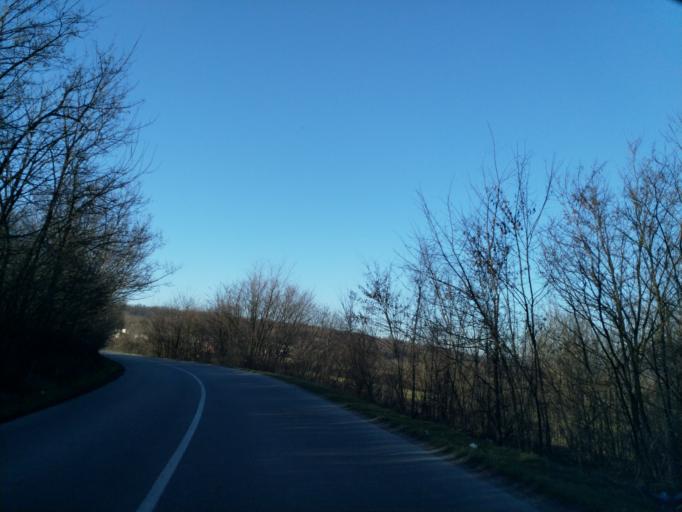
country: RS
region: Central Serbia
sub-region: Pomoravski Okrug
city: Paracin
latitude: 43.8738
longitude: 21.4712
